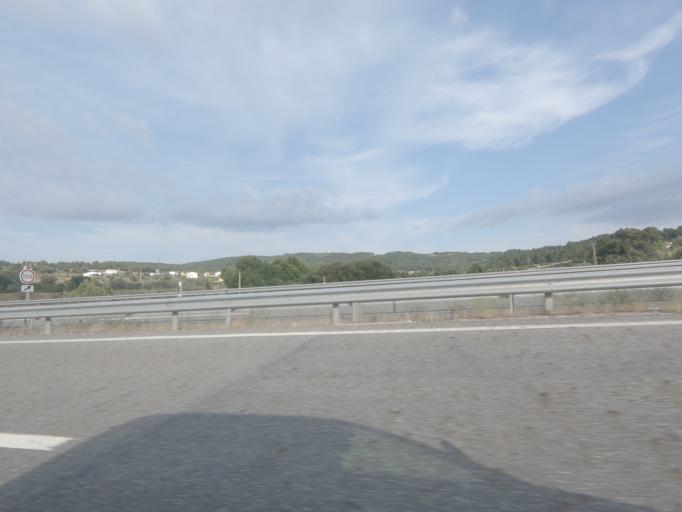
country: PT
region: Vila Real
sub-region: Boticas
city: Boticas
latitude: 41.6634
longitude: -7.5737
